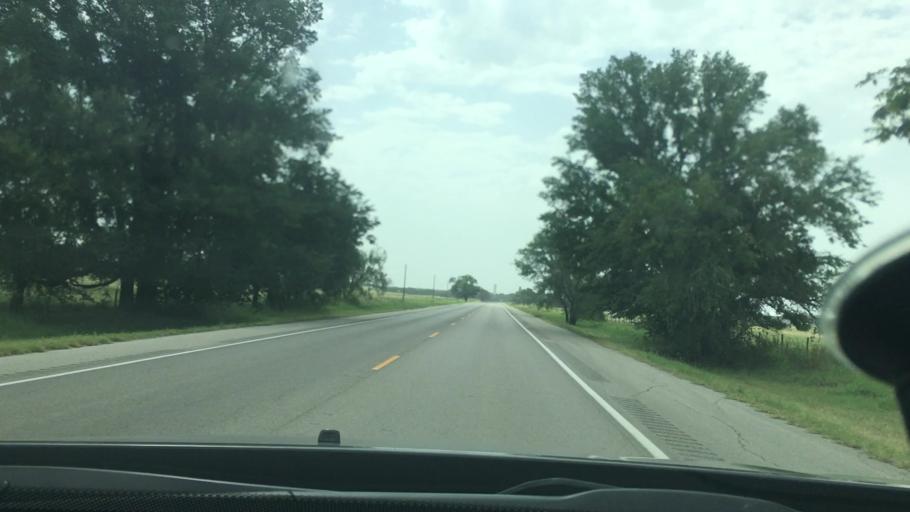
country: US
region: Oklahoma
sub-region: Garvin County
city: Pauls Valley
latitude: 34.8399
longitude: -97.2713
